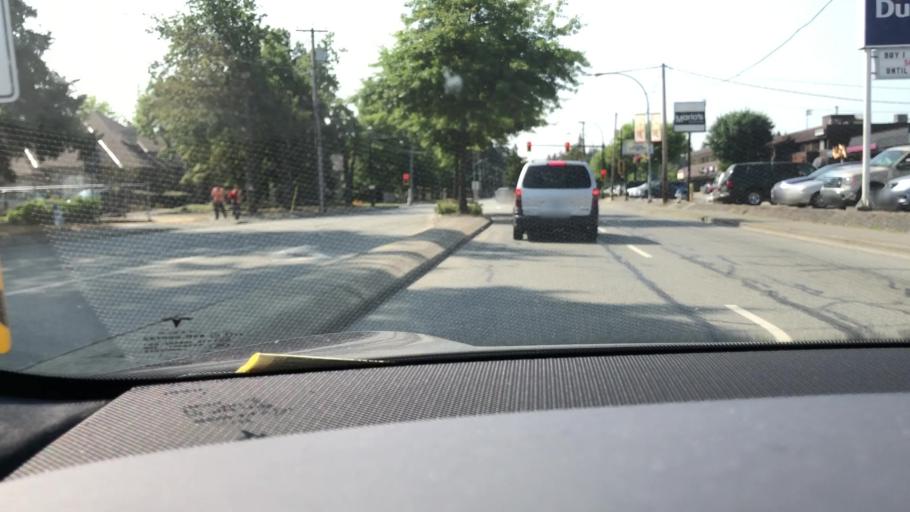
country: US
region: Washington
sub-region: Whatcom County
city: Point Roberts
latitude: 49.0235
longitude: -123.0688
